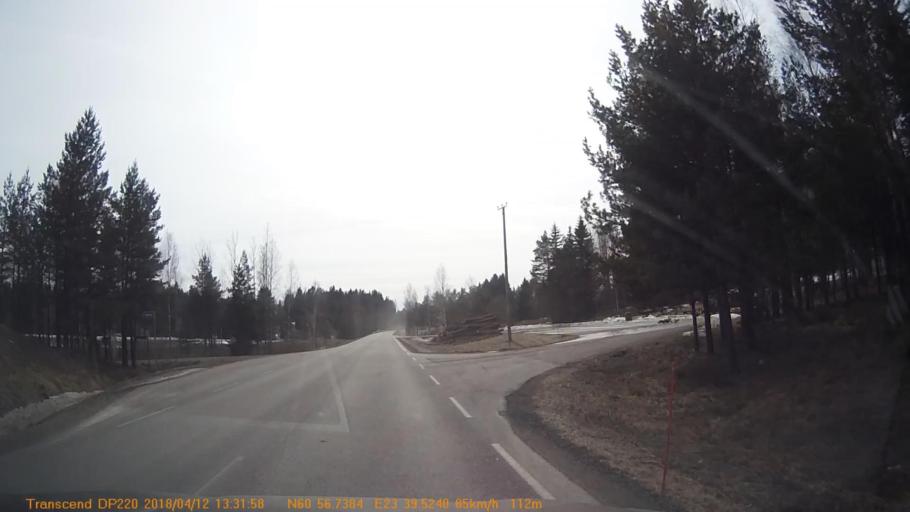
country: FI
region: Haeme
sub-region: Forssa
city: Forssa
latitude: 60.9454
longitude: 23.6586
